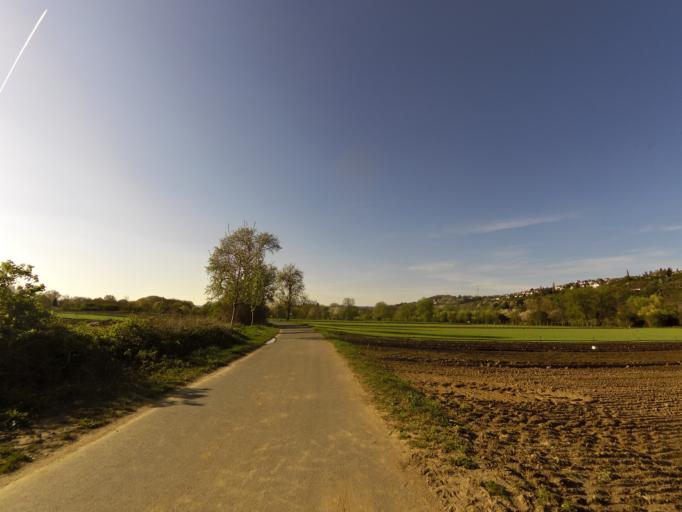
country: DE
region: Rheinland-Pfalz
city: Weitersburg
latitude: 50.4014
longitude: 7.5910
